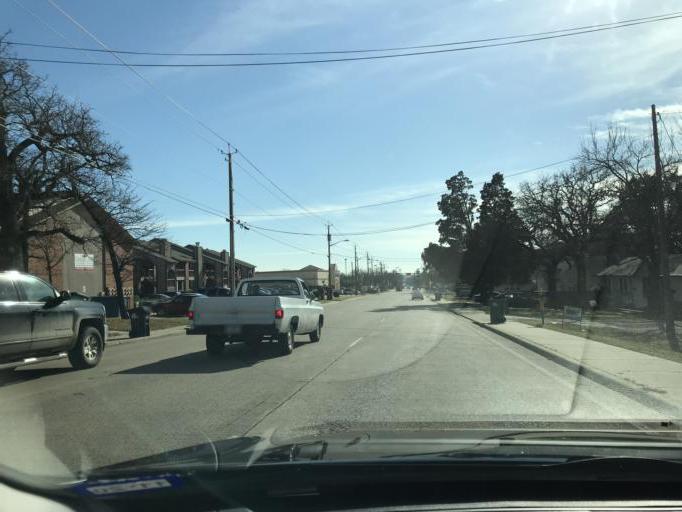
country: US
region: Texas
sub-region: Denton County
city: Denton
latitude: 33.2334
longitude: -97.1334
